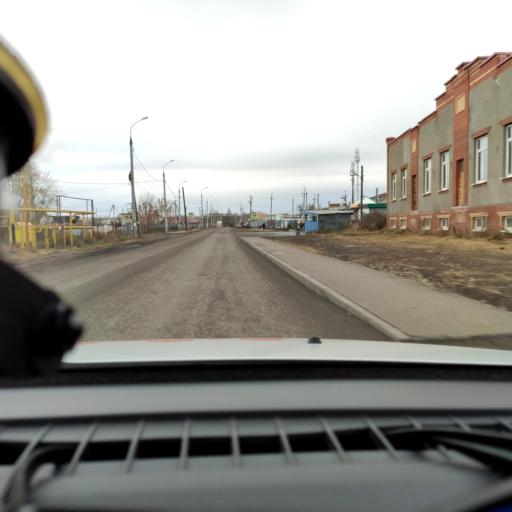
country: RU
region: Samara
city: Samara
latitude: 53.1333
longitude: 50.2358
